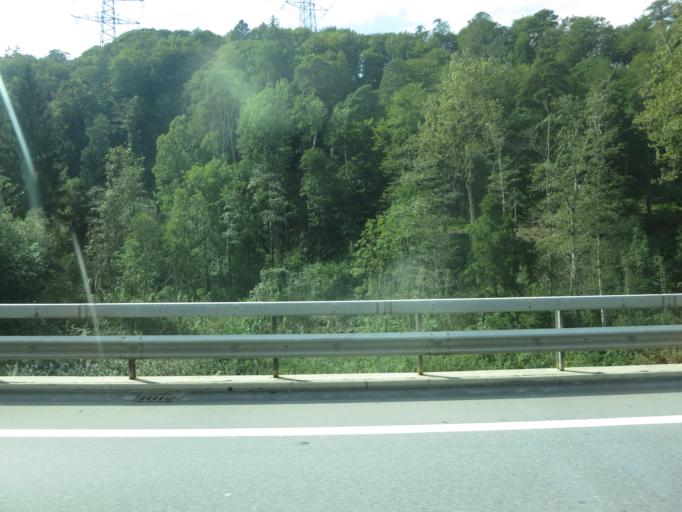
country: CH
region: Grisons
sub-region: Imboden District
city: Bonaduz
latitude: 46.8086
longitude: 9.4121
